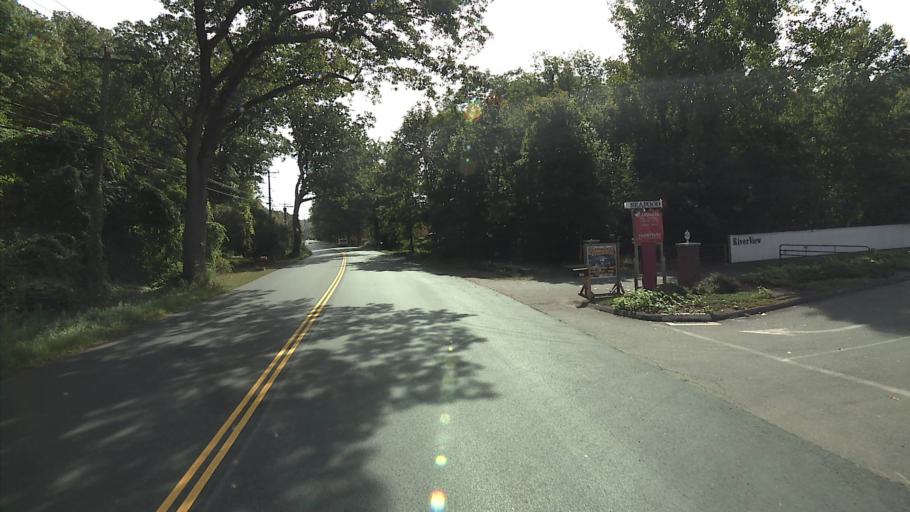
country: US
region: Connecticut
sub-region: Fairfield County
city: Shelton
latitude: 41.3533
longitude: -73.1350
